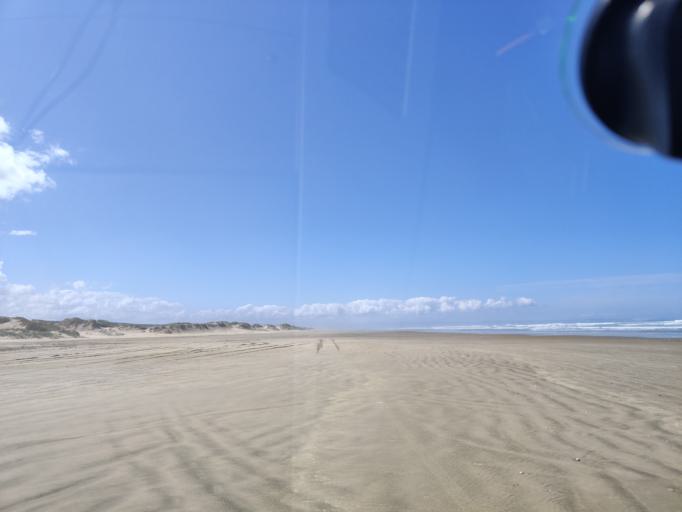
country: NZ
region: Northland
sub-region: Far North District
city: Ahipara
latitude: -34.9009
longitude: 173.0856
